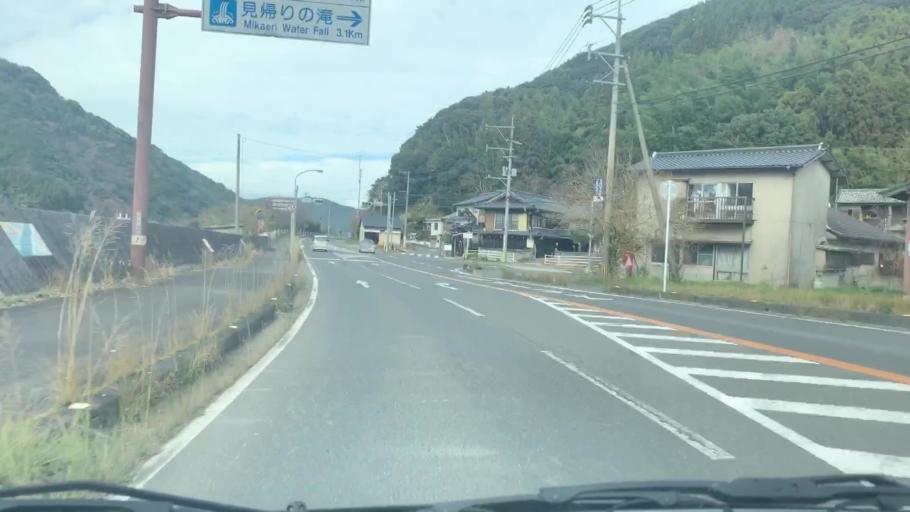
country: JP
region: Saga Prefecture
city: Karatsu
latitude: 33.3634
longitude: 130.0092
